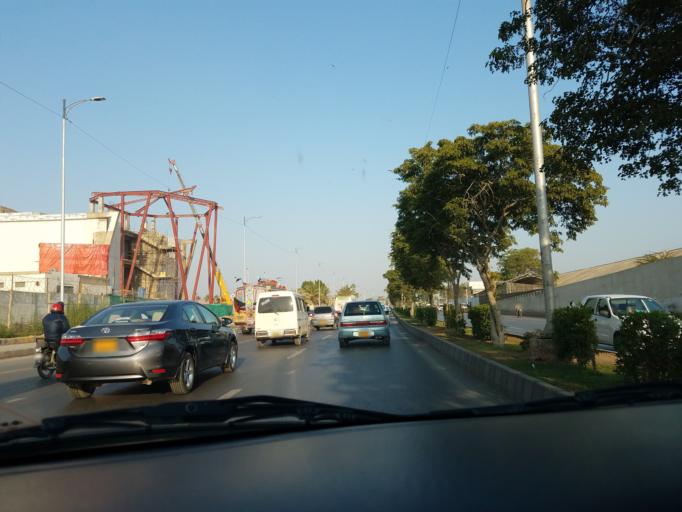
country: PK
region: Sindh
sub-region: Karachi District
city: Karachi
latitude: 24.8853
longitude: 67.1189
